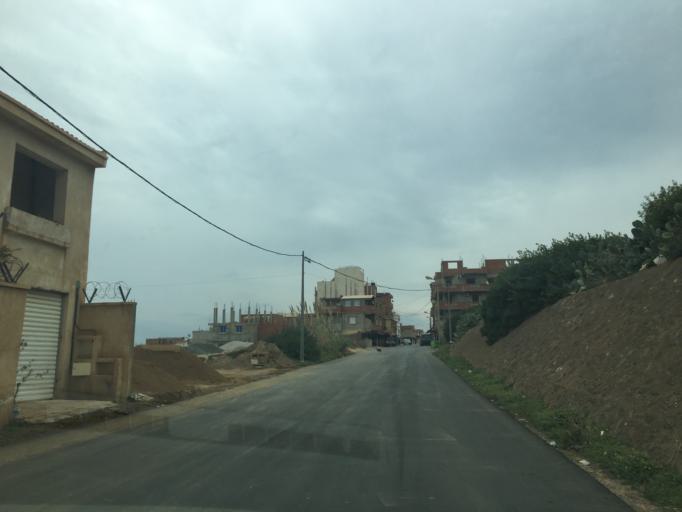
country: DZ
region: Tipaza
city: Tipasa
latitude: 36.6414
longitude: 2.3452
